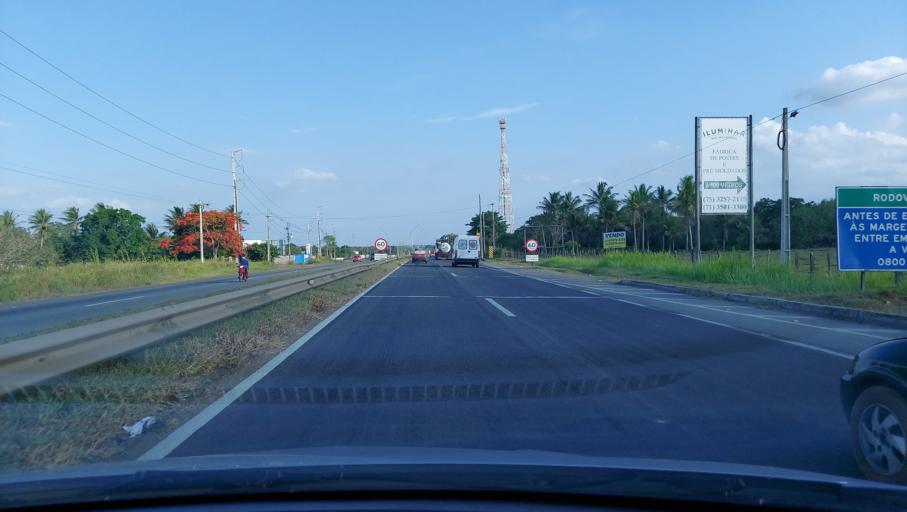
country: BR
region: Bahia
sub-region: Conceicao Do Jacuipe
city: Conceicao do Jacuipe
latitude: -12.3748
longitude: -38.8062
